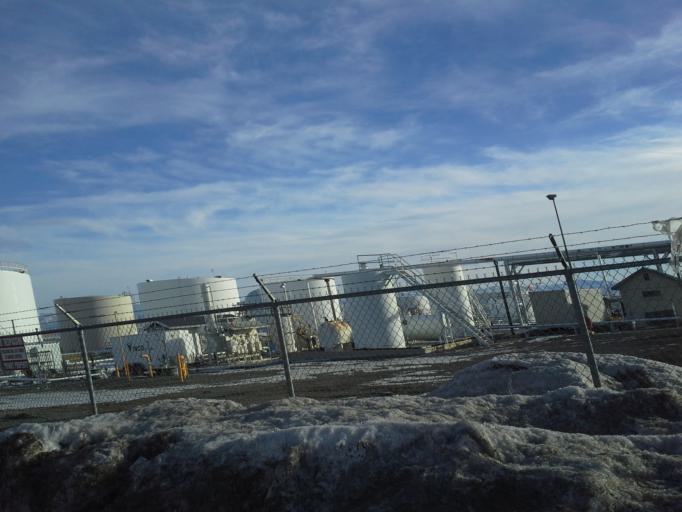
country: US
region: Montana
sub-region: Lewis and Clark County
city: Helena
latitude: 46.5921
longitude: -111.9836
